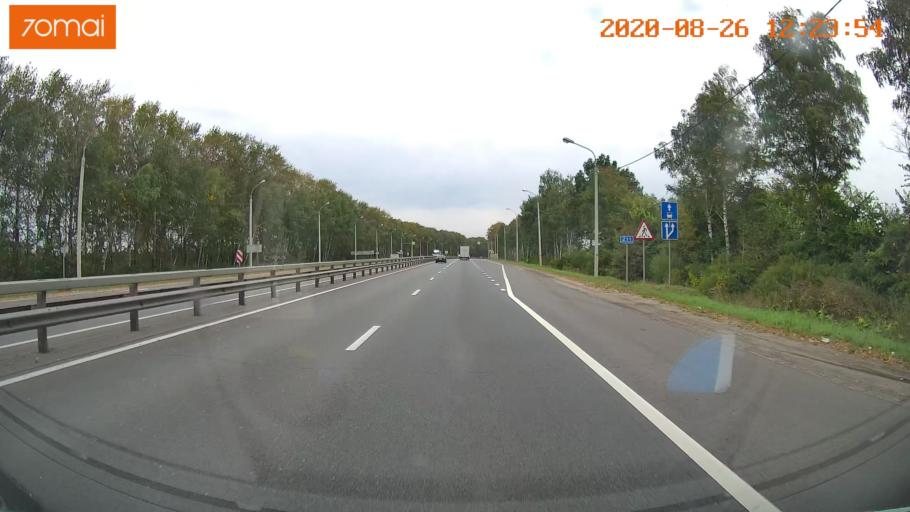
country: RU
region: Rjazan
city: Murmino
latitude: 54.5084
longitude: 39.9023
